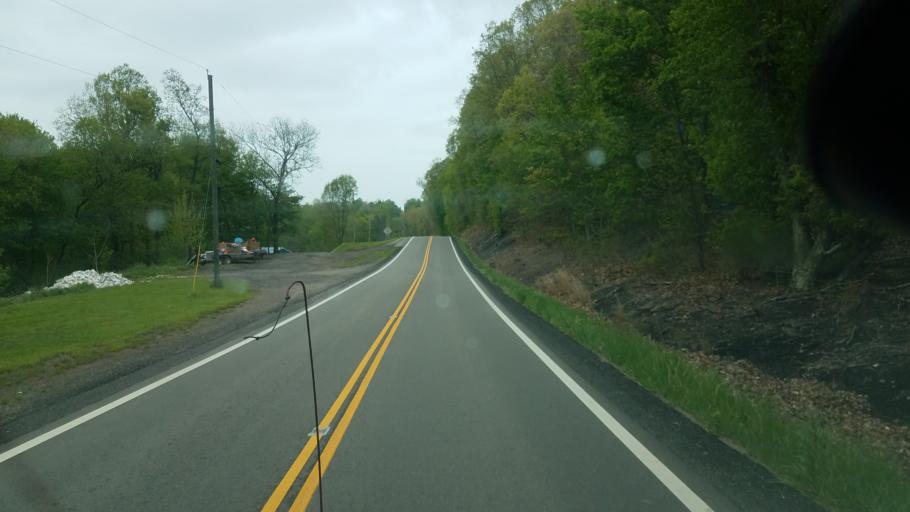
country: US
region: Ohio
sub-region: Coshocton County
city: West Lafayette
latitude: 40.2233
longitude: -81.7961
